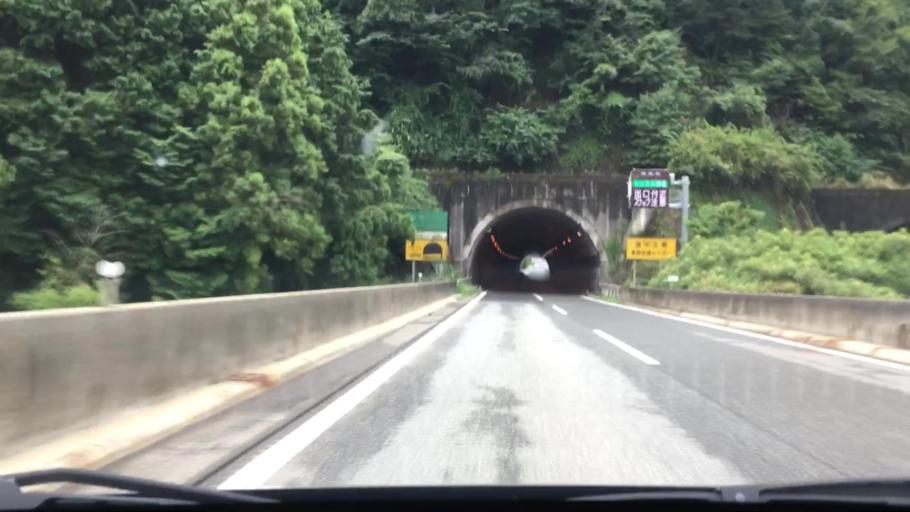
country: JP
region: Hiroshima
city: Hiroshima-shi
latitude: 34.5275
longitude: 132.4325
